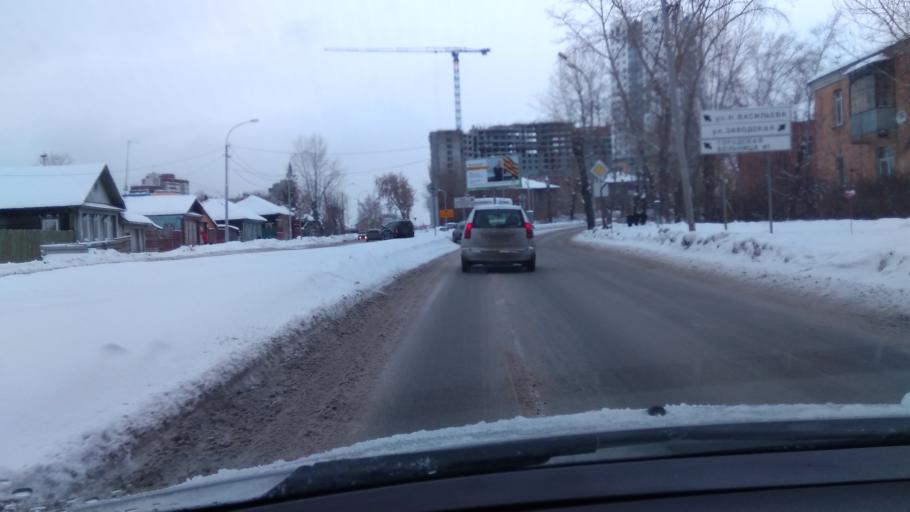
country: RU
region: Sverdlovsk
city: Sovkhoznyy
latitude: 56.8208
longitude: 60.5536
